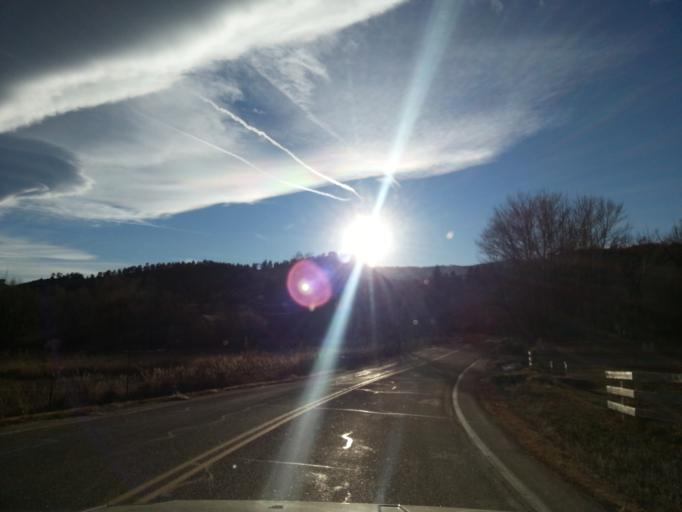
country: US
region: Colorado
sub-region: Larimer County
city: Loveland
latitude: 40.4821
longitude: -105.2121
